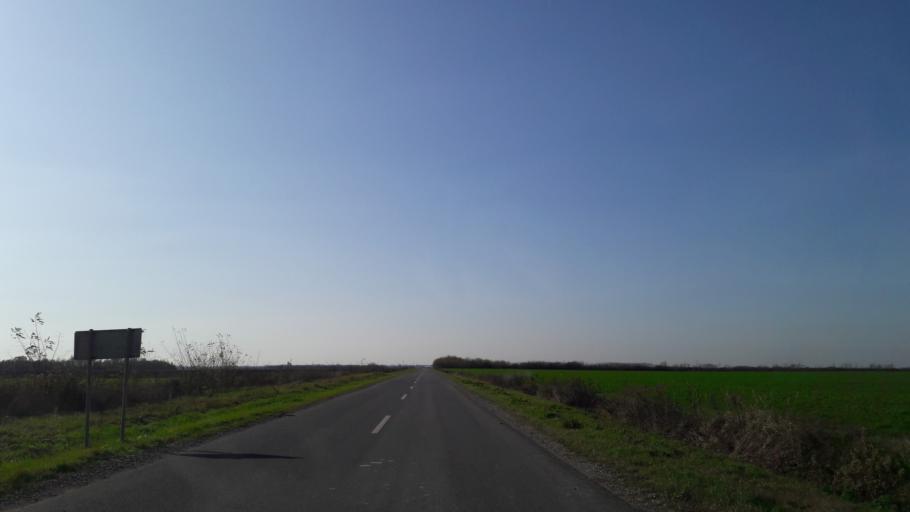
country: HR
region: Osjecko-Baranjska
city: Tenja
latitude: 45.4820
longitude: 18.7157
